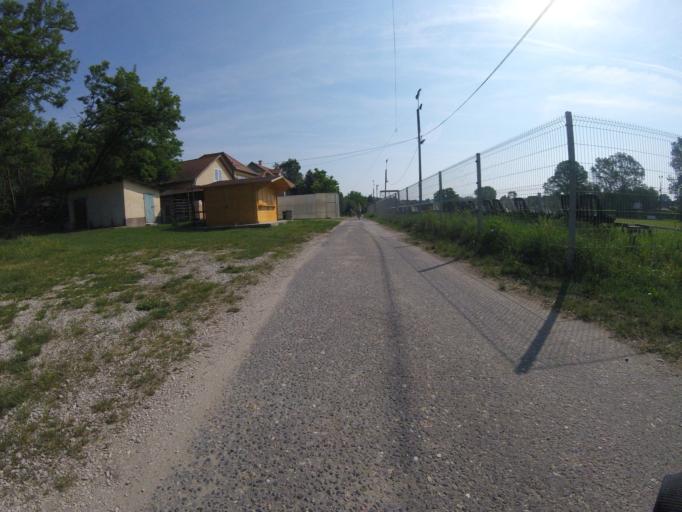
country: HU
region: Tolna
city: Bolcske
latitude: 46.7392
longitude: 18.9566
